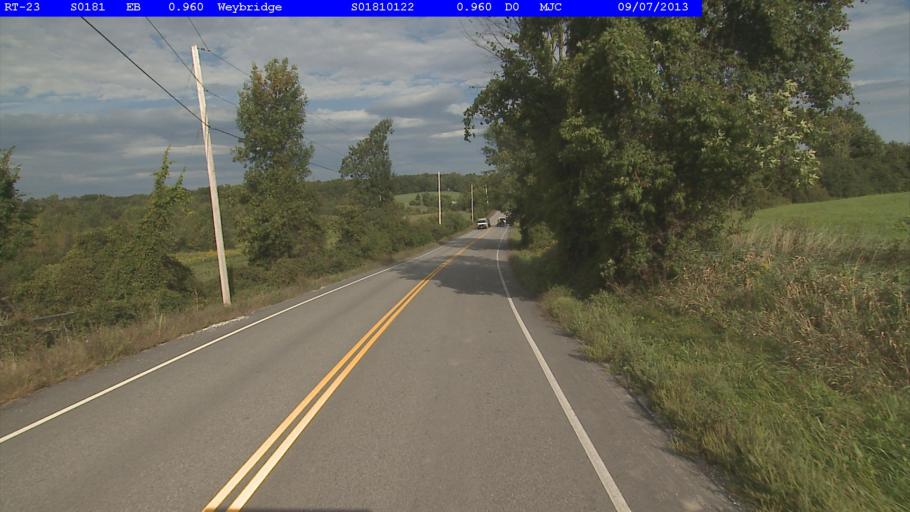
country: US
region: Vermont
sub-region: Addison County
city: Middlebury (village)
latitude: 44.0274
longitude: -73.1976
